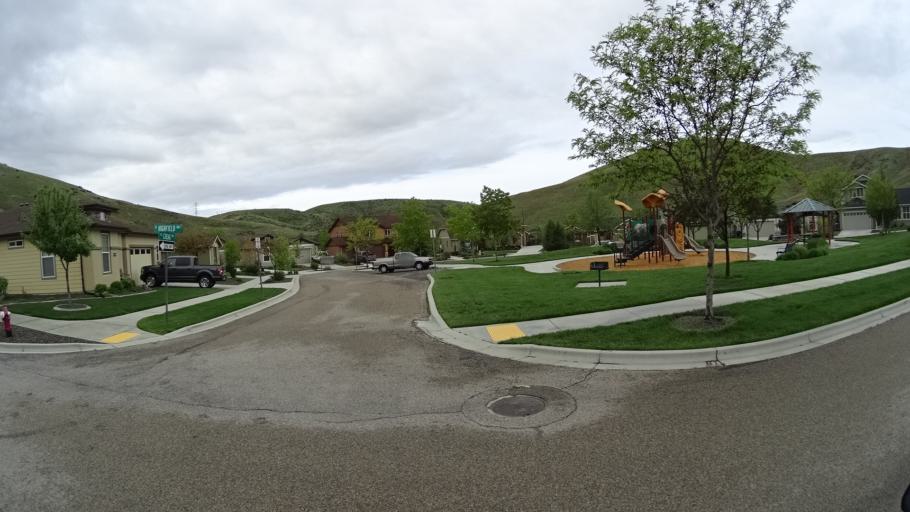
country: US
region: Idaho
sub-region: Ada County
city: Eagle
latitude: 43.7676
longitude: -116.2630
